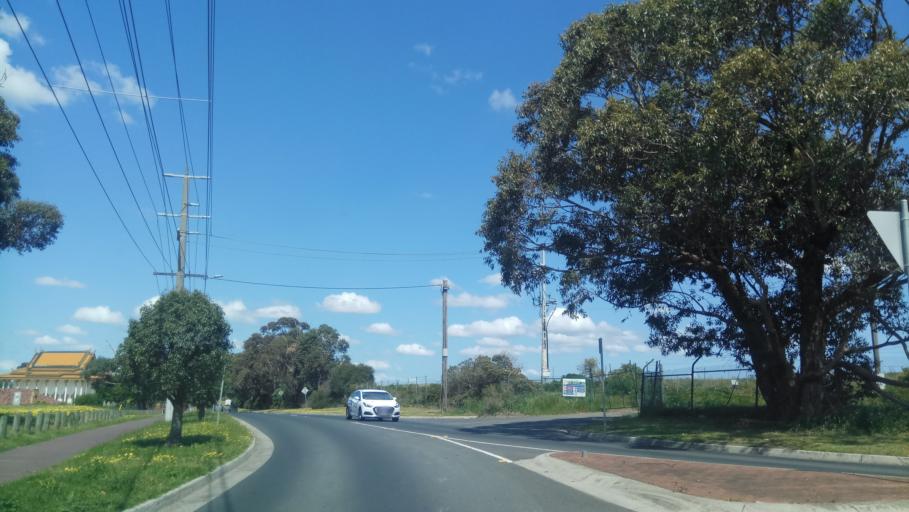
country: AU
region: Victoria
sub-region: Greater Dandenong
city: Springvale South
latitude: -37.9722
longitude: 145.1432
